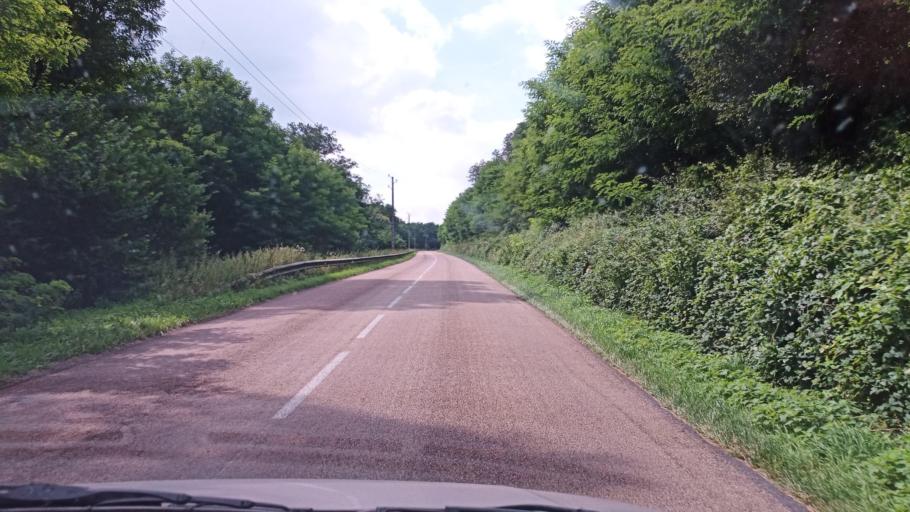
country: FR
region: Bourgogne
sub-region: Departement de l'Yonne
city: Villeneuve-sur-Yonne
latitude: 48.0660
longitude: 3.2614
